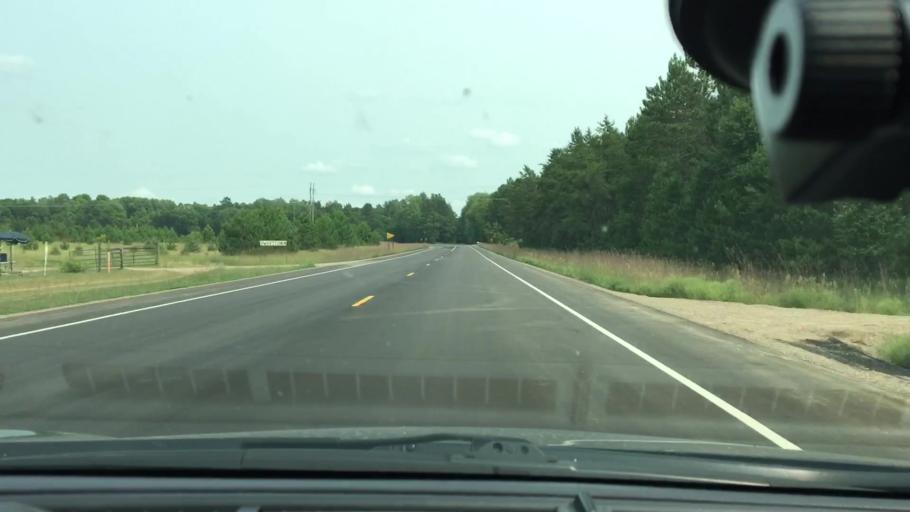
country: US
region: Minnesota
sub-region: Crow Wing County
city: Nisswa
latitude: 46.5299
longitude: -94.2331
